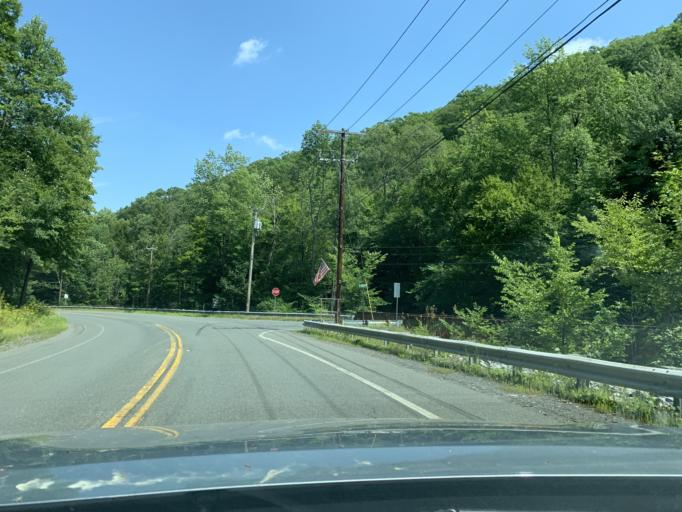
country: US
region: Massachusetts
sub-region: Berkshire County
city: Becket
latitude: 42.2708
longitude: -73.0008
